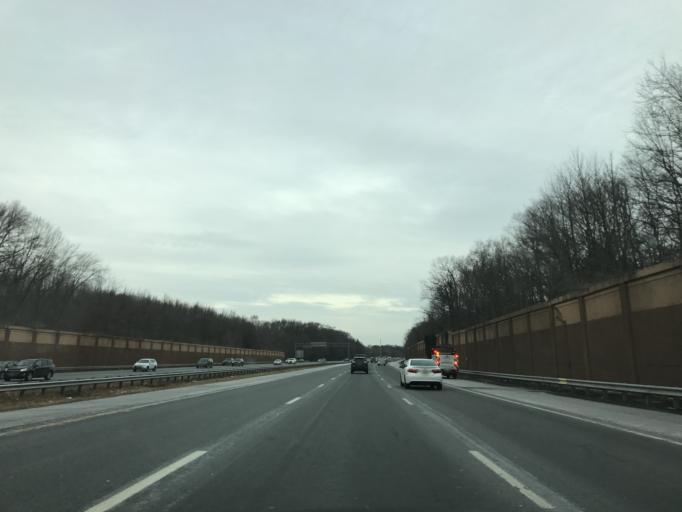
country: US
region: New Jersey
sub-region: Camden County
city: Kingston Estates
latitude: 39.9233
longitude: -74.9774
